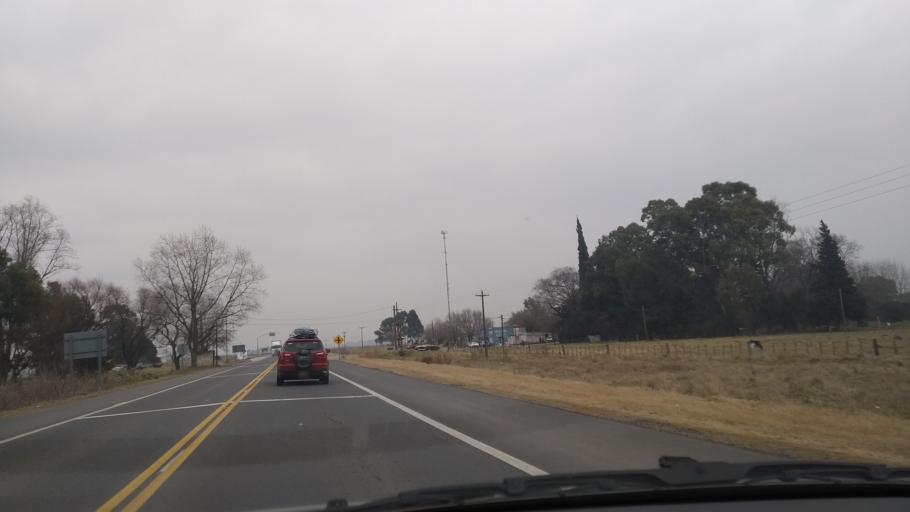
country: AR
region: Buenos Aires
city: Olavarria
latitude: -36.9892
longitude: -60.3096
